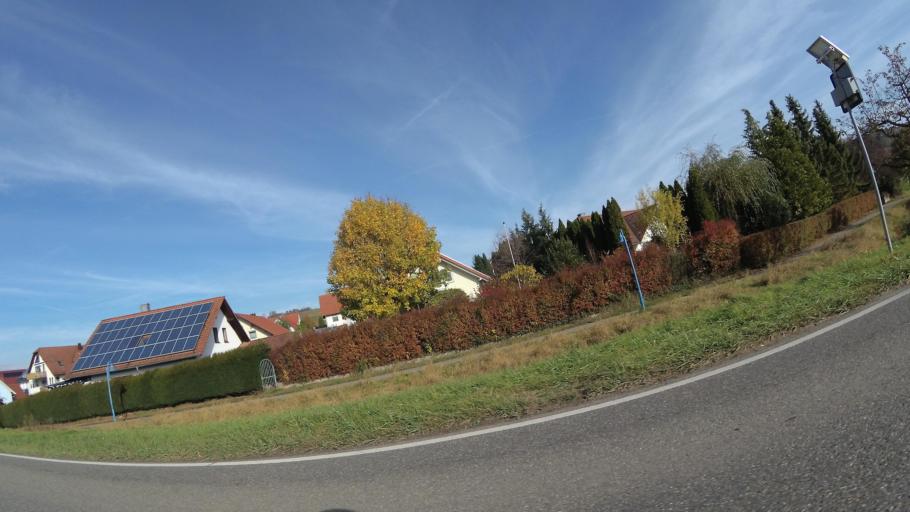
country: DE
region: Baden-Wuerttemberg
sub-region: Regierungsbezirk Stuttgart
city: Gundelsheim
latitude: 49.2795
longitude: 9.1685
